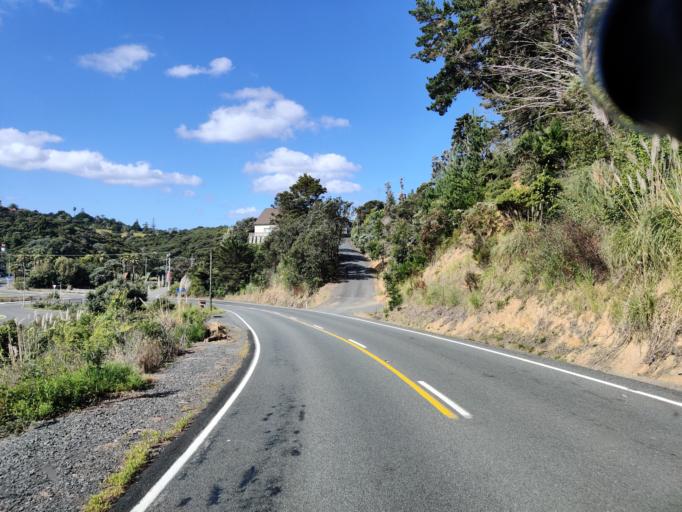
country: NZ
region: Northland
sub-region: Whangarei
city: Ngunguru
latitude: -35.6120
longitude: 174.5240
